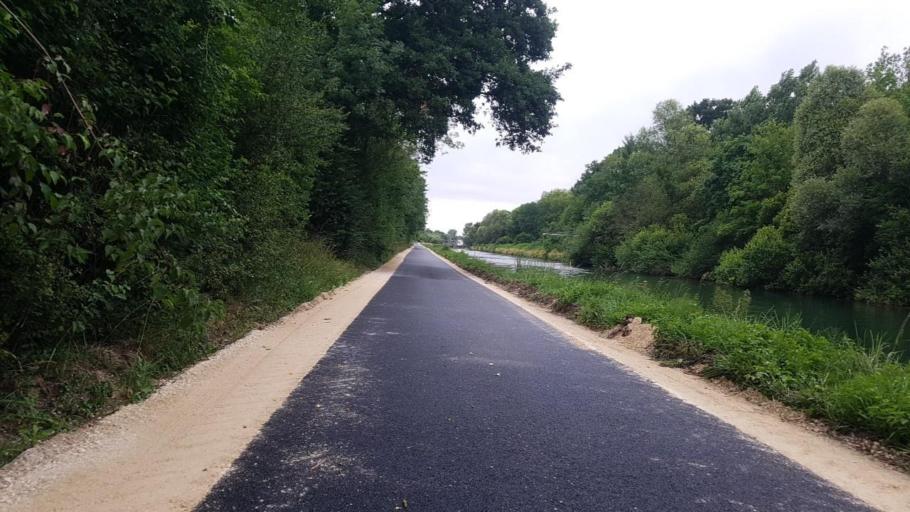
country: FR
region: Champagne-Ardenne
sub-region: Departement de la Marne
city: Vitry-le-Francois
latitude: 48.8053
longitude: 4.5223
